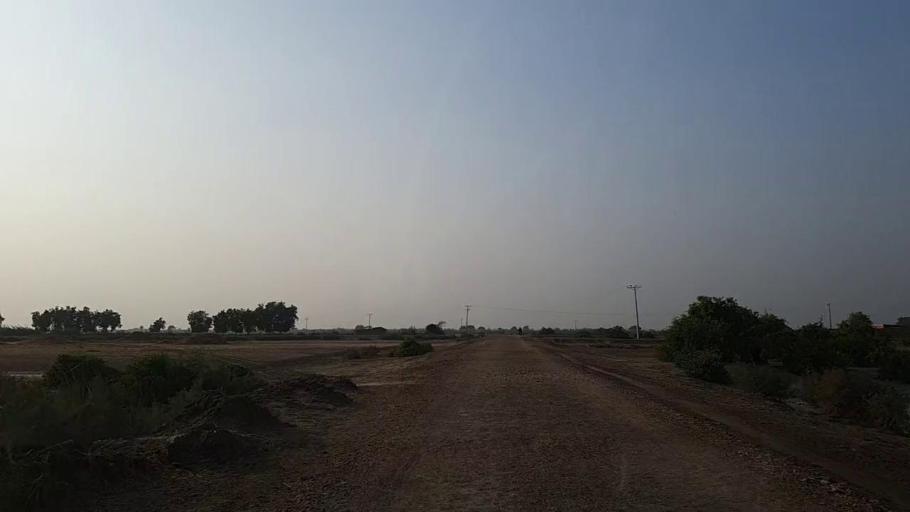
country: PK
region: Sindh
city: Thatta
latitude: 24.6933
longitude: 67.7863
